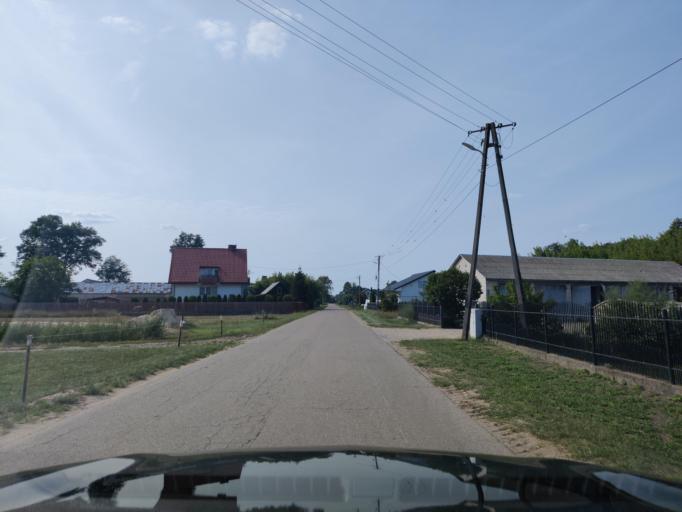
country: PL
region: Masovian Voivodeship
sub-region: Powiat pultuski
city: Obryte
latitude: 52.7644
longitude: 21.2904
